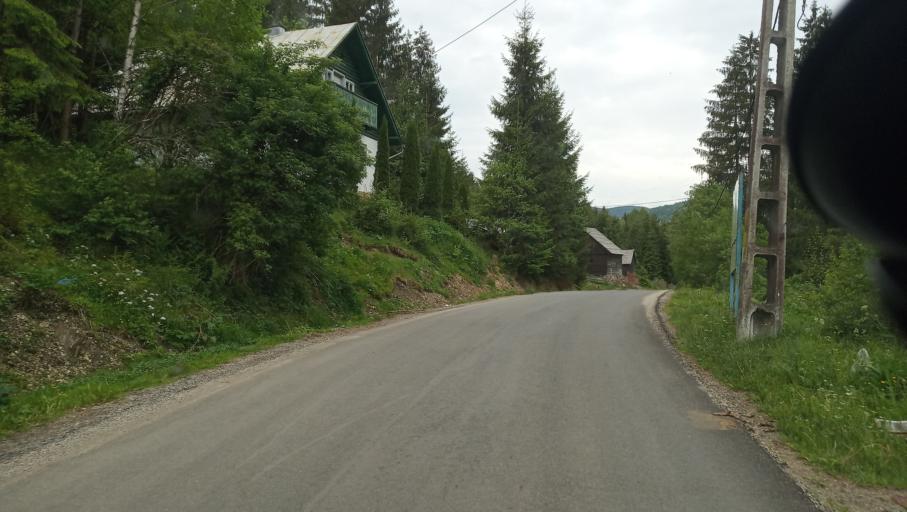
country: RO
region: Alba
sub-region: Comuna Horea
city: Horea
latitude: 46.4997
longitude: 22.9414
